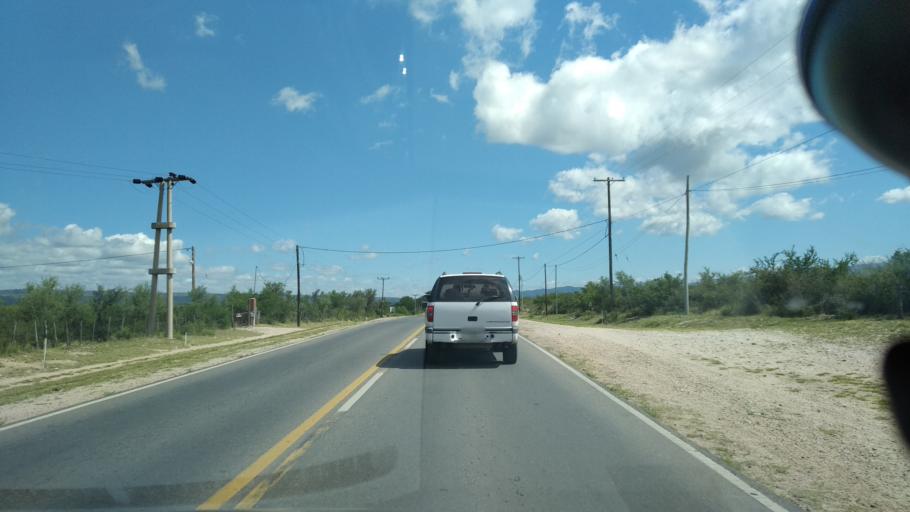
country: AR
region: Cordoba
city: Mina Clavero
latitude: -31.7845
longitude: -64.9987
